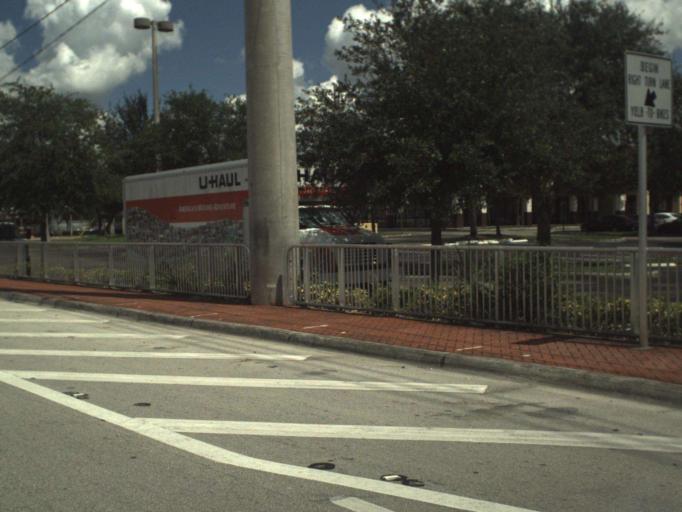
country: US
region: Florida
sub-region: Miami-Dade County
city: Andover
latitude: 25.9717
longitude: -80.2059
